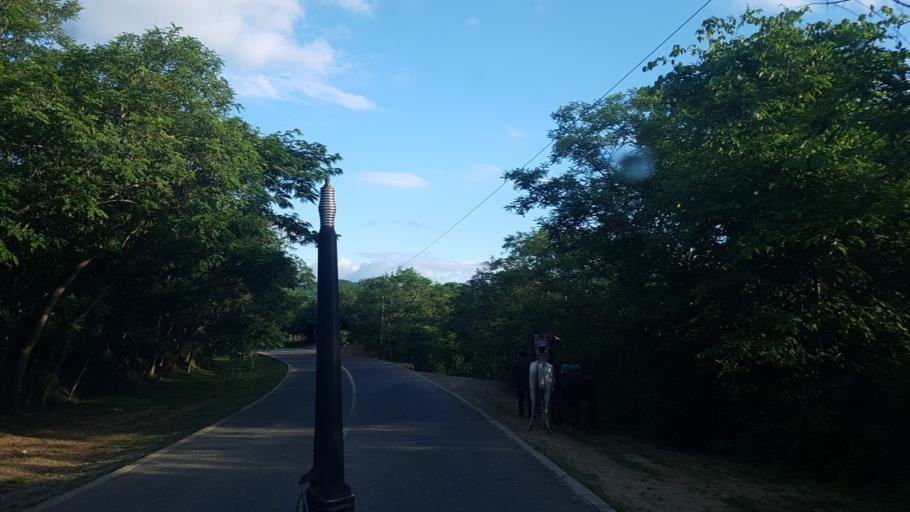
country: NI
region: Nueva Segovia
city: Ocotal
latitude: 13.6442
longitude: -86.6028
